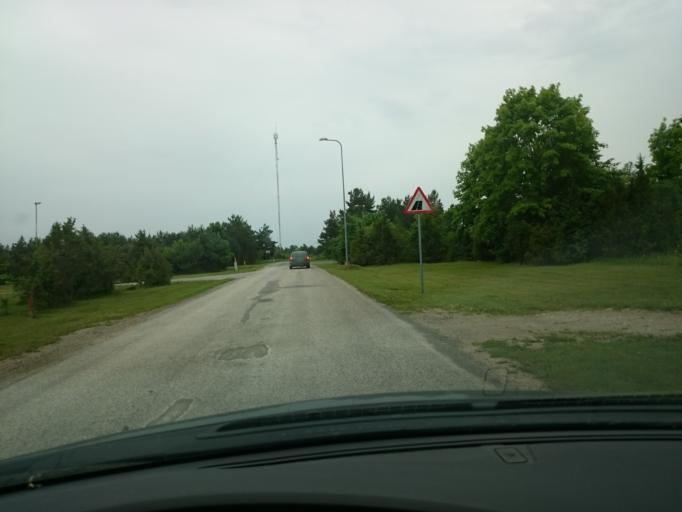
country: EE
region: Saare
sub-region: Orissaare vald
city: Orissaare
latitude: 58.6024
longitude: 23.2362
